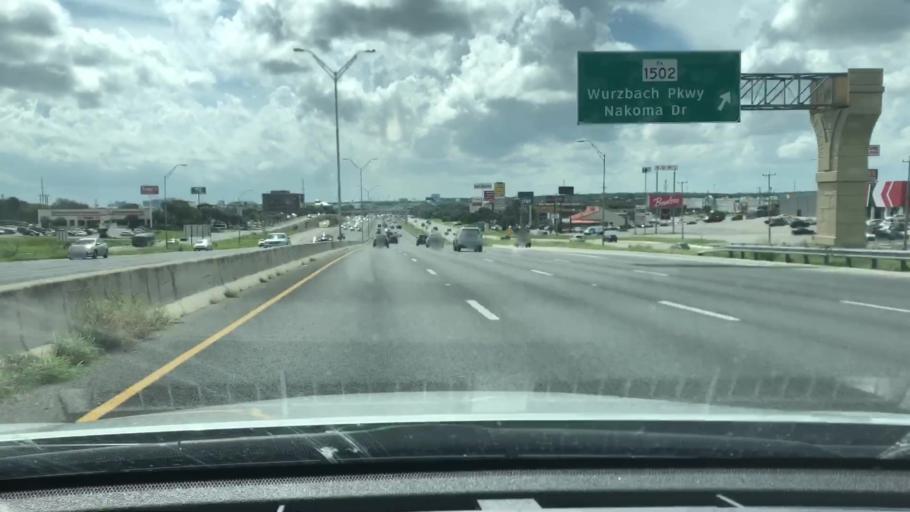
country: US
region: Texas
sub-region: Bexar County
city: Hollywood Park
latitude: 29.5637
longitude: -98.4816
